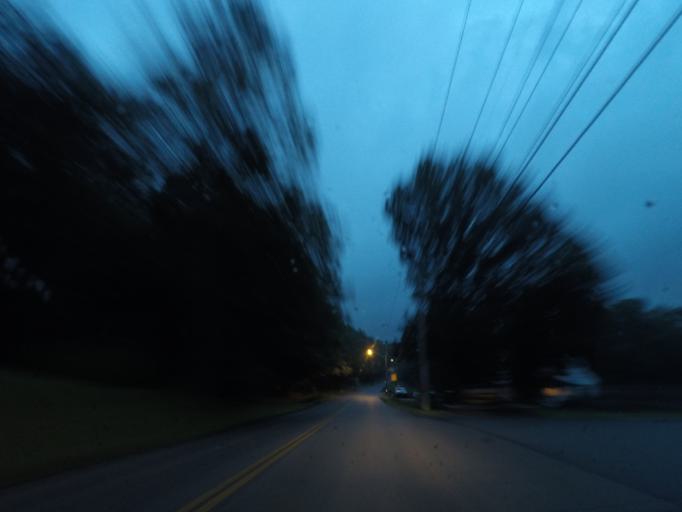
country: US
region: Massachusetts
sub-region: Worcester County
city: Southbridge
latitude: 42.0750
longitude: -72.0567
